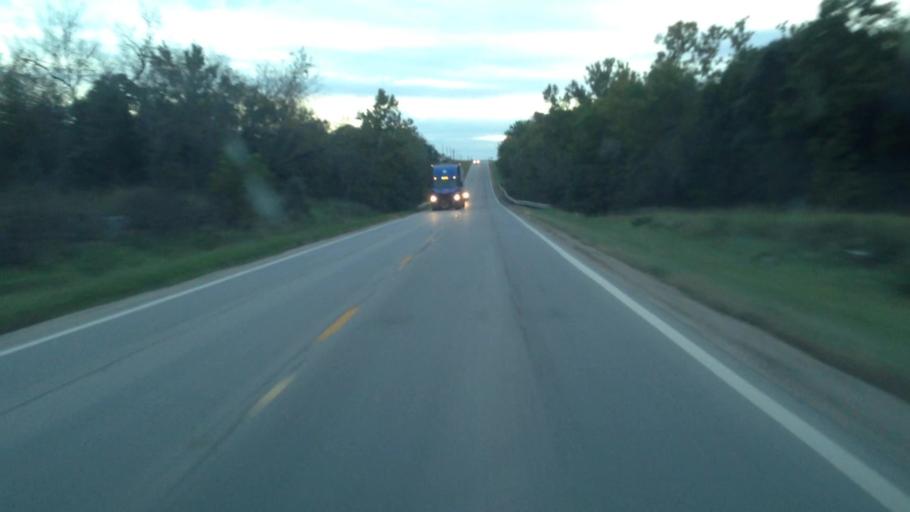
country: US
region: Kansas
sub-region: Anderson County
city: Garnett
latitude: 38.2346
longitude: -95.2481
